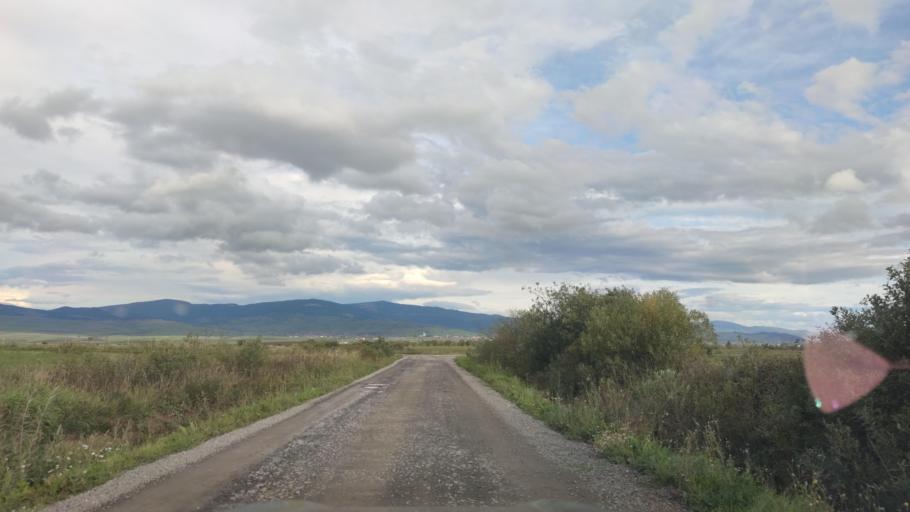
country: RO
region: Harghita
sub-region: Comuna Remetea
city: Remetea
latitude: 46.8159
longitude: 25.4209
